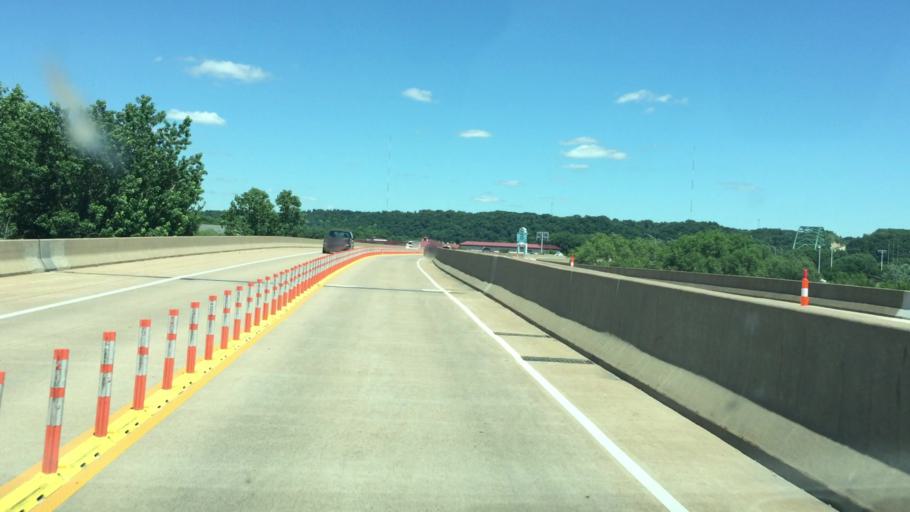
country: US
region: Iowa
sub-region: Dubuque County
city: Dubuque
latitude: 42.5148
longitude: -90.6511
